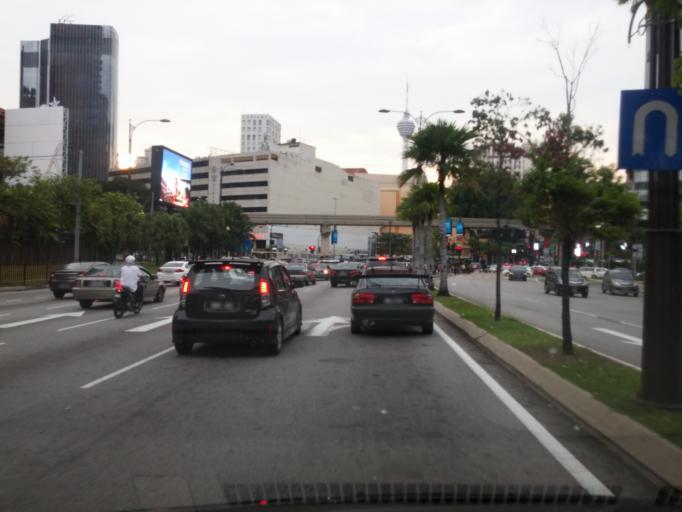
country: MY
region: Kuala Lumpur
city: Kuala Lumpur
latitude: 3.1429
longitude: 101.7129
